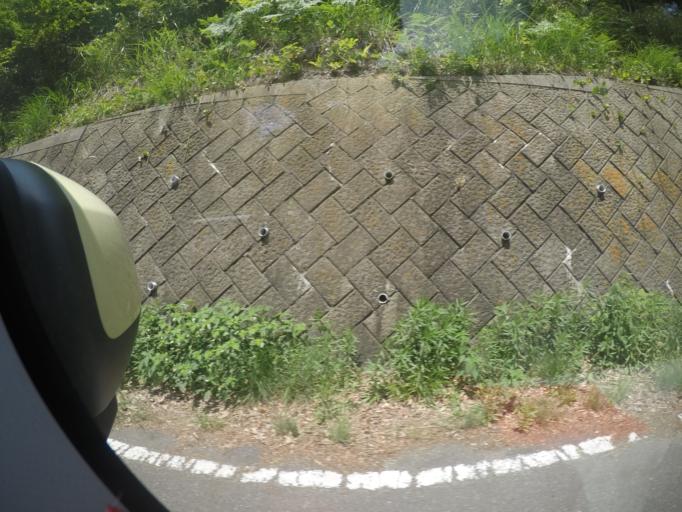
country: JP
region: Ibaraki
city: Iwase
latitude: 36.3316
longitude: 140.1183
